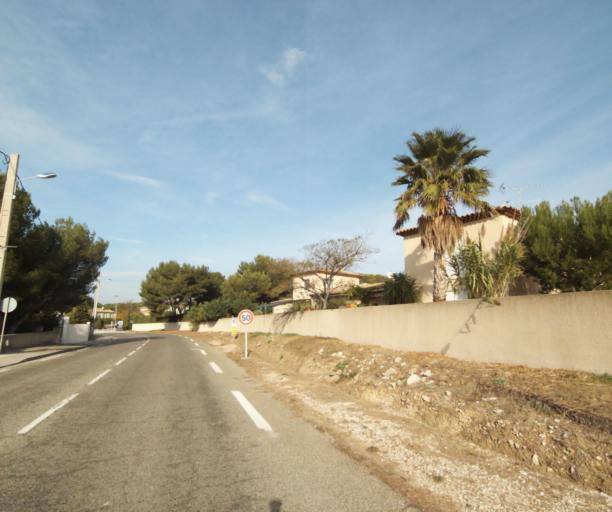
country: FR
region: Provence-Alpes-Cote d'Azur
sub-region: Departement des Bouches-du-Rhone
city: Carry-le-Rouet
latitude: 43.3318
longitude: 5.1653
